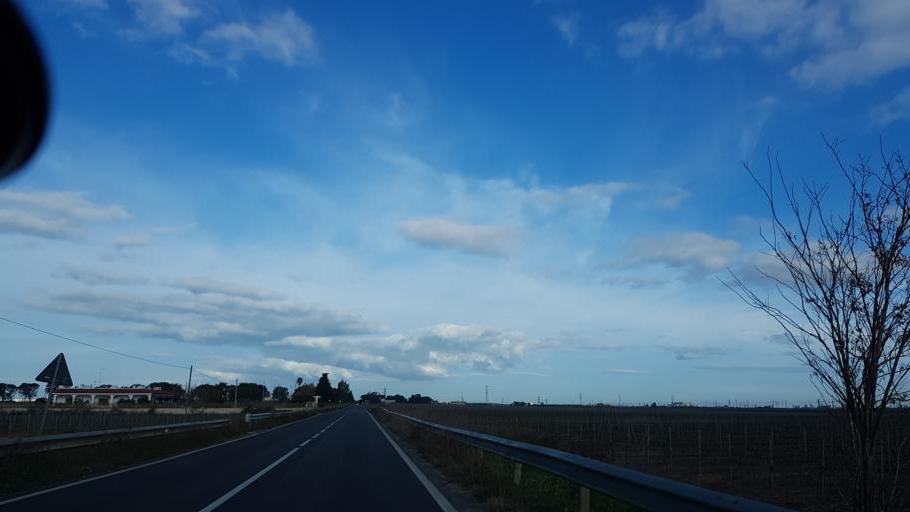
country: IT
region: Apulia
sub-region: Provincia di Brindisi
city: La Rosa
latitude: 40.5754
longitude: 17.9665
